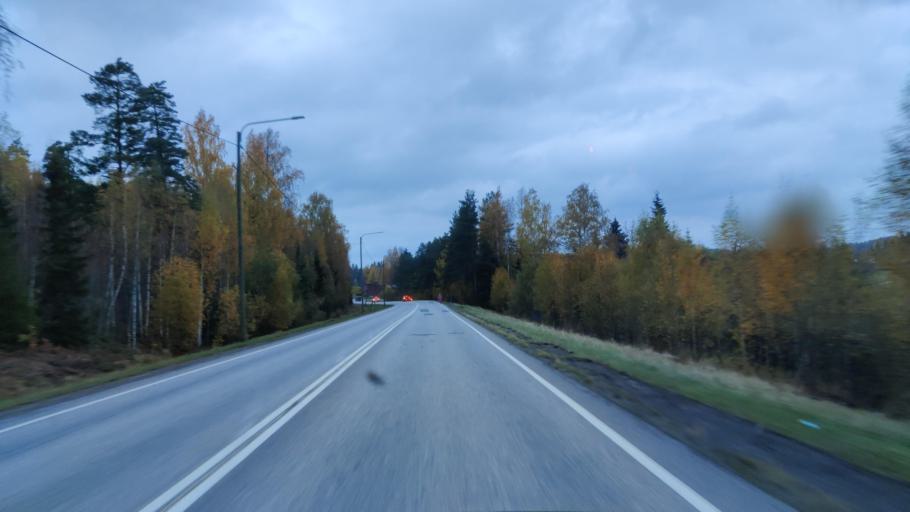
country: FI
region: Uusimaa
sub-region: Helsinki
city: Vihti
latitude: 60.3415
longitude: 24.1959
